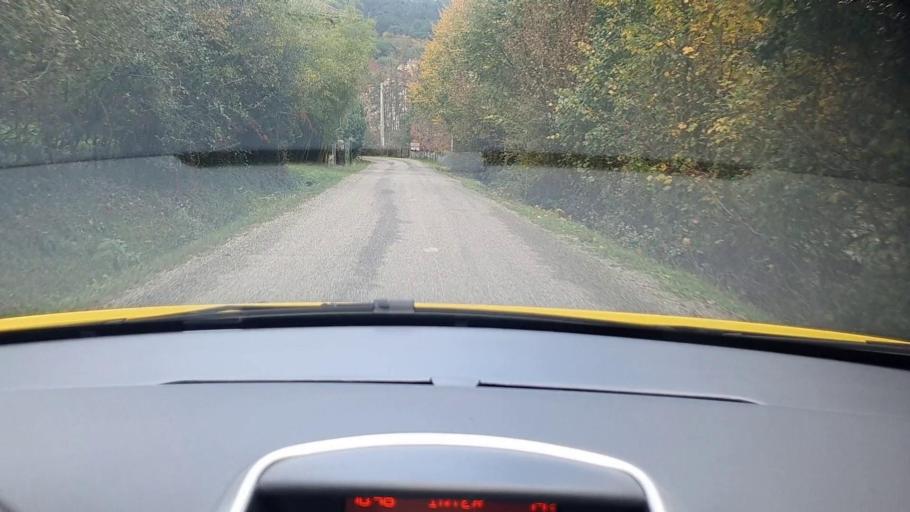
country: FR
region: Languedoc-Roussillon
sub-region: Departement du Gard
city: Lasalle
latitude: 44.0454
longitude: 3.8487
